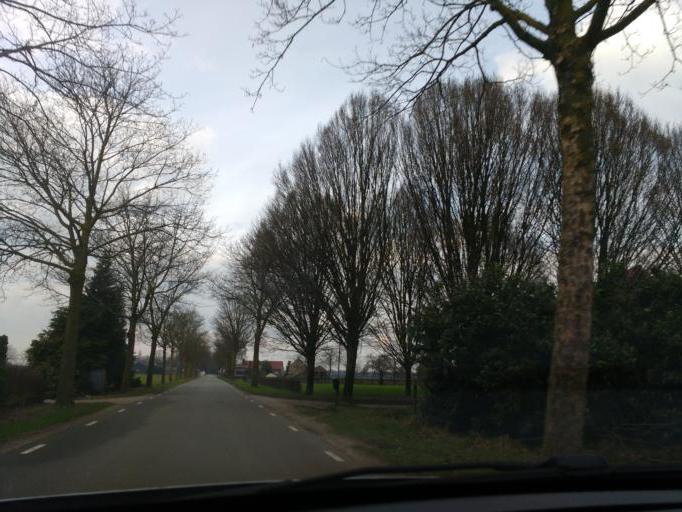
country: NL
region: North Brabant
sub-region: Gemeente Boxmeer
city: Overloon
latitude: 51.5771
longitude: 5.9690
